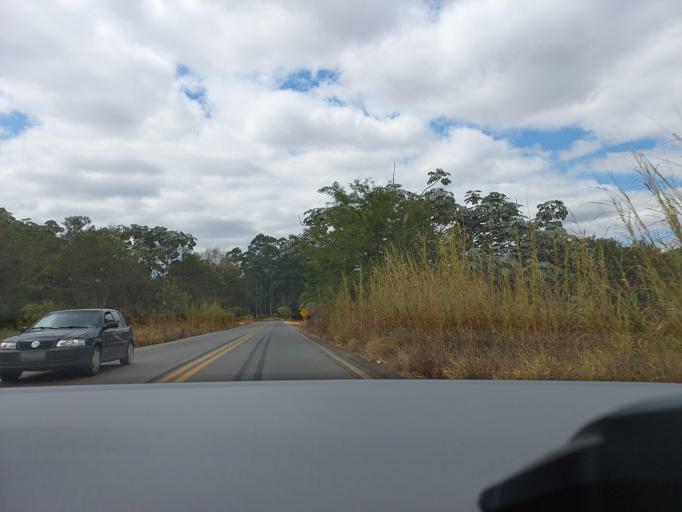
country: BR
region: Minas Gerais
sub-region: Vicosa
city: Vicosa
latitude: -20.8404
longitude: -42.7076
